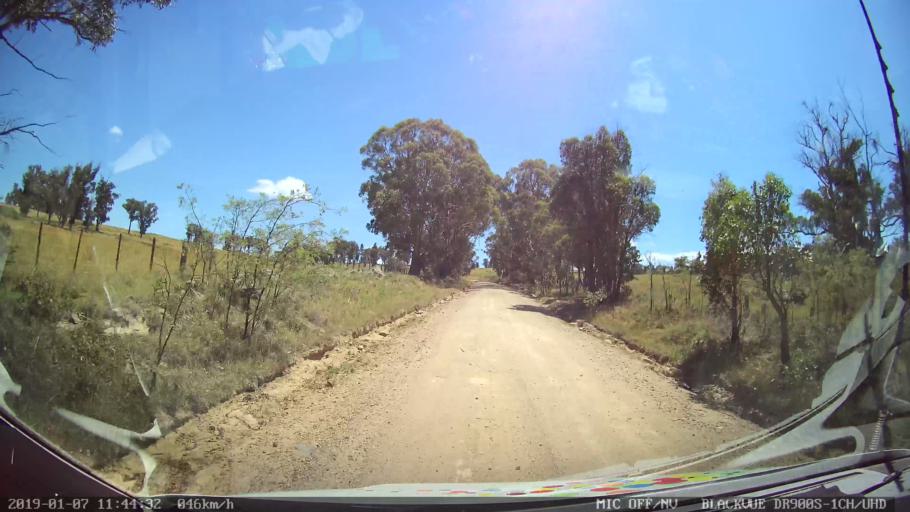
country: AU
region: New South Wales
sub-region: Guyra
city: Guyra
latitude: -30.3520
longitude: 151.6064
